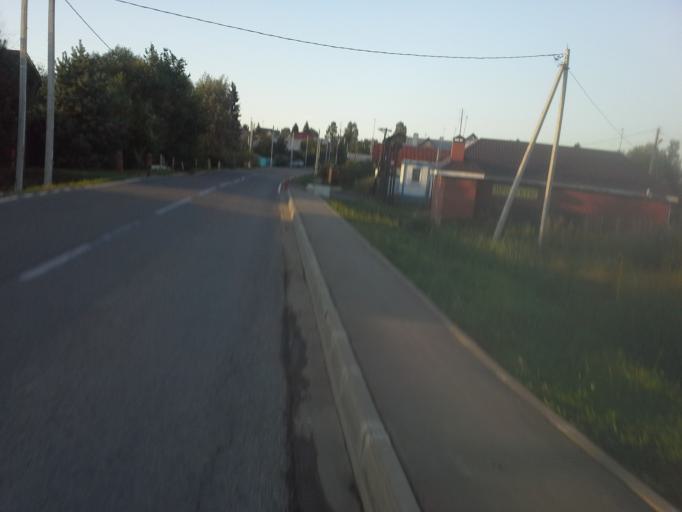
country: RU
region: Moskovskaya
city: Selyatino
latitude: 55.4982
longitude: 36.9238
